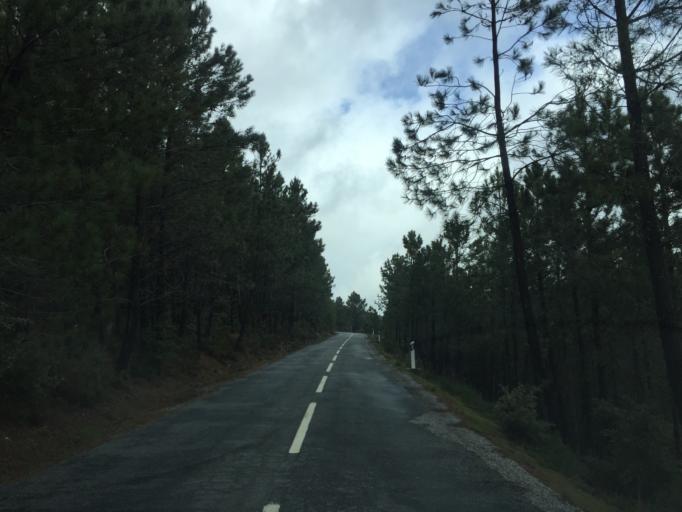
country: PT
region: Guarda
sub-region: Seia
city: Seia
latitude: 40.3292
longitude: -7.7149
